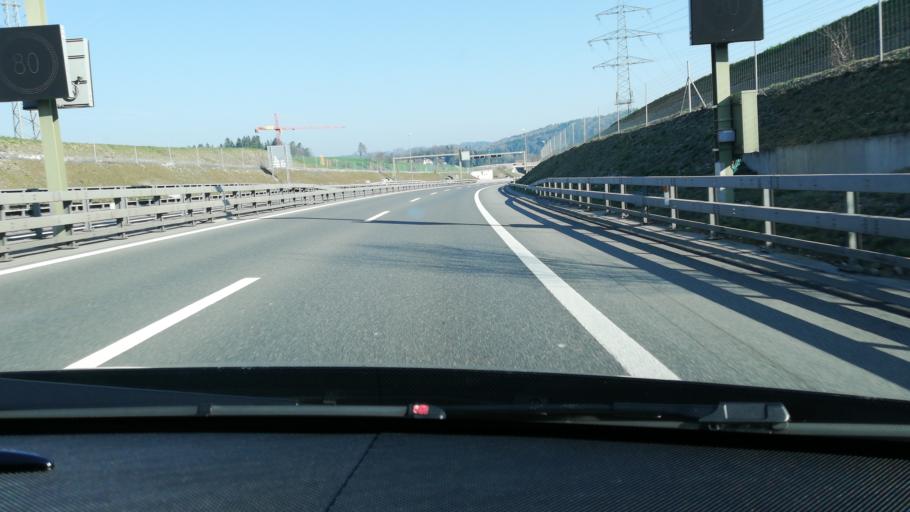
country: CH
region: Zurich
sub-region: Bezirk Affoltern
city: Ottenbach
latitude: 47.2860
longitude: 8.4240
